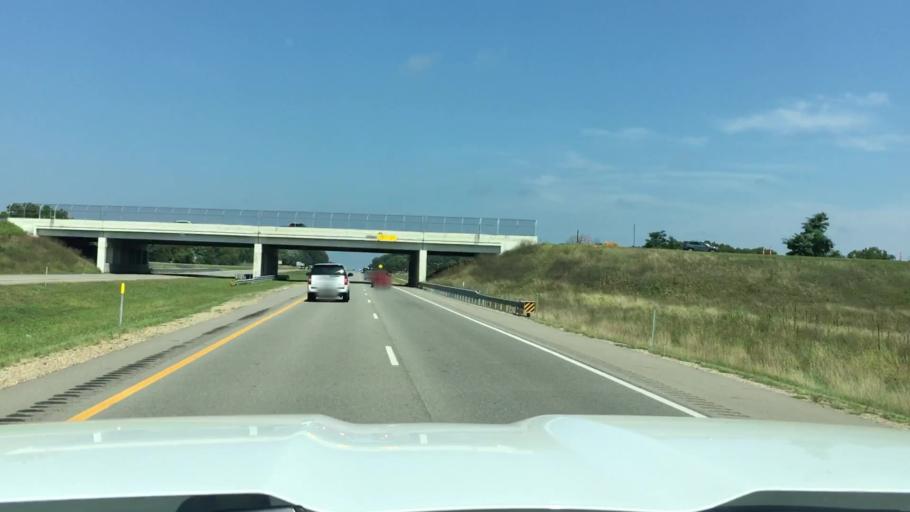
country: US
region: Michigan
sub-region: Kalamazoo County
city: Portage
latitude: 42.1985
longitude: -85.6457
